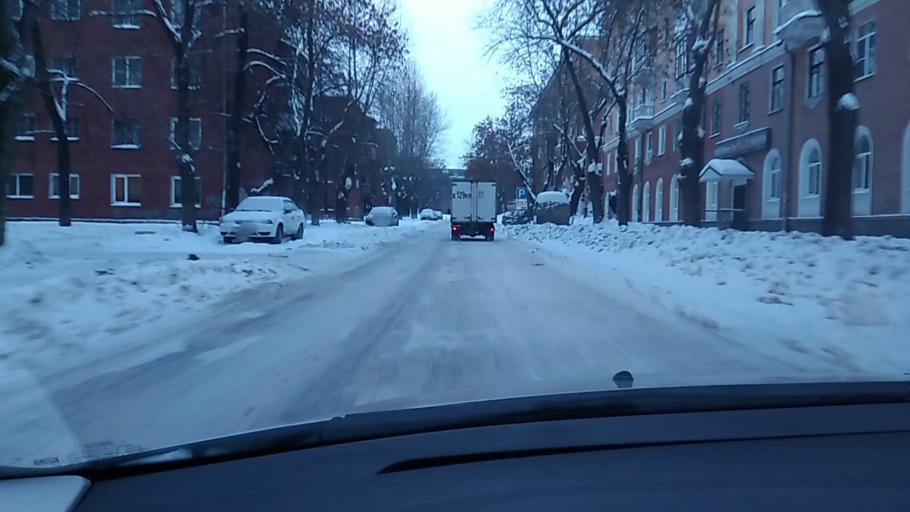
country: RU
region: Sverdlovsk
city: Yekaterinburg
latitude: 56.8908
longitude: 60.5935
